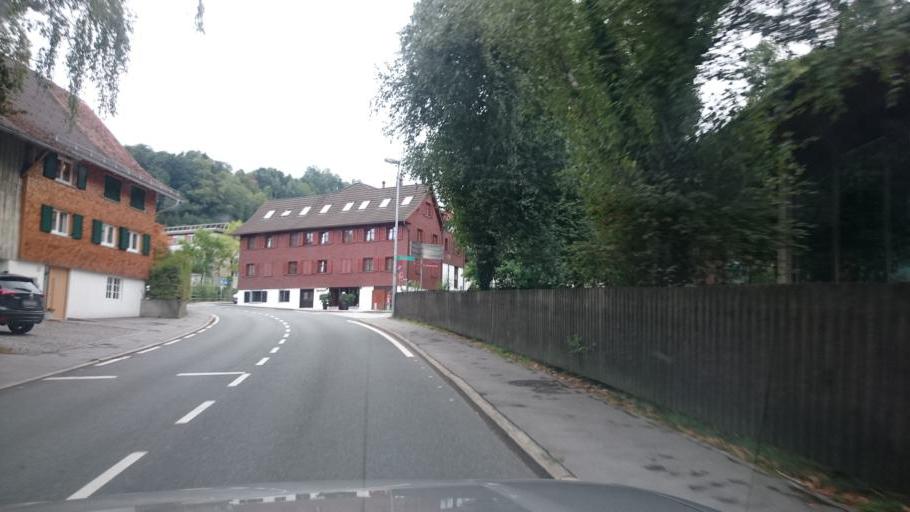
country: AT
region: Vorarlberg
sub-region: Politischer Bezirk Dornbirn
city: Dornbirn
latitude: 47.4092
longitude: 9.7530
